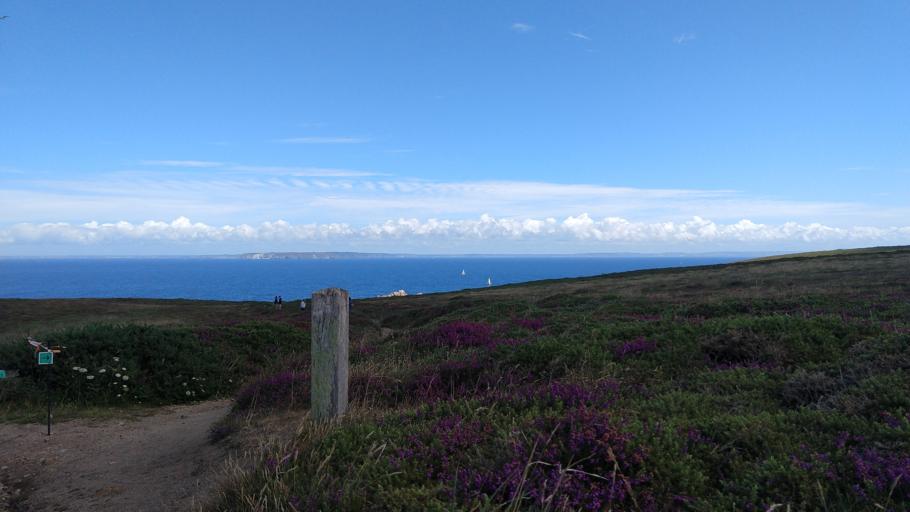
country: FR
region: Brittany
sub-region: Departement du Finistere
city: Esquibien
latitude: 48.0780
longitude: -4.5861
